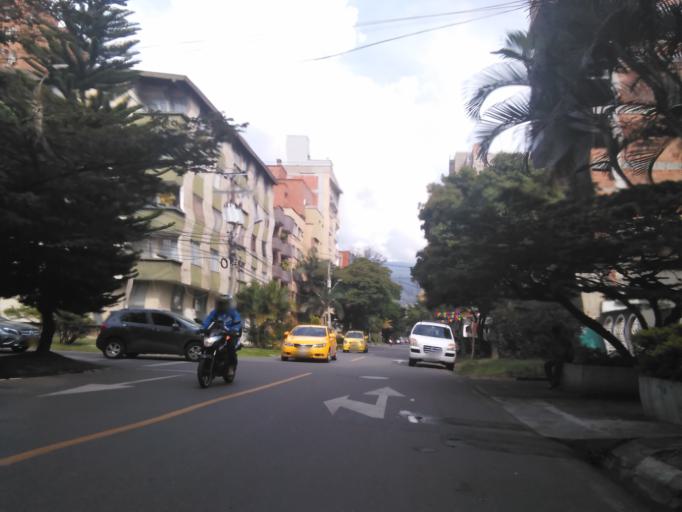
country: CO
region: Antioquia
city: Medellin
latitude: 6.2399
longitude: -75.5829
